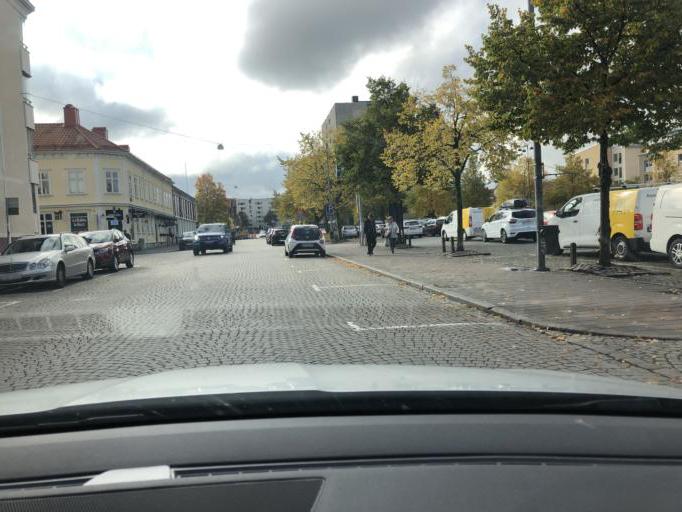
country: SE
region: Joenkoeping
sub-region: Jonkopings Kommun
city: Jonkoping
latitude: 57.7816
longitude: 14.1570
